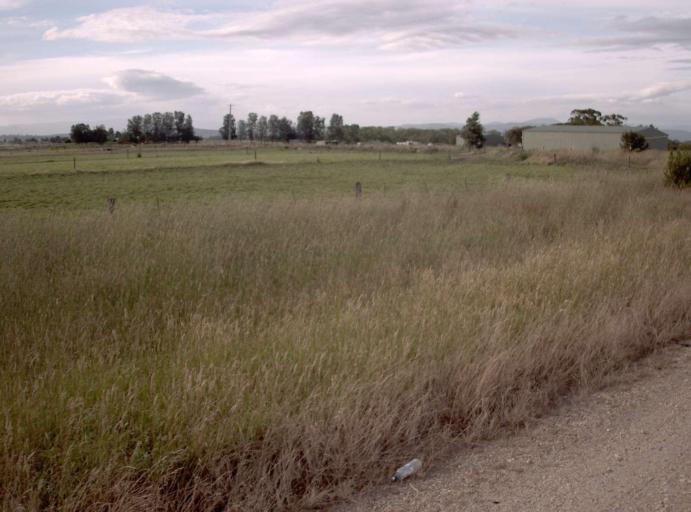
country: AU
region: Victoria
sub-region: Wellington
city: Heyfield
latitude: -37.9860
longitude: 146.8872
